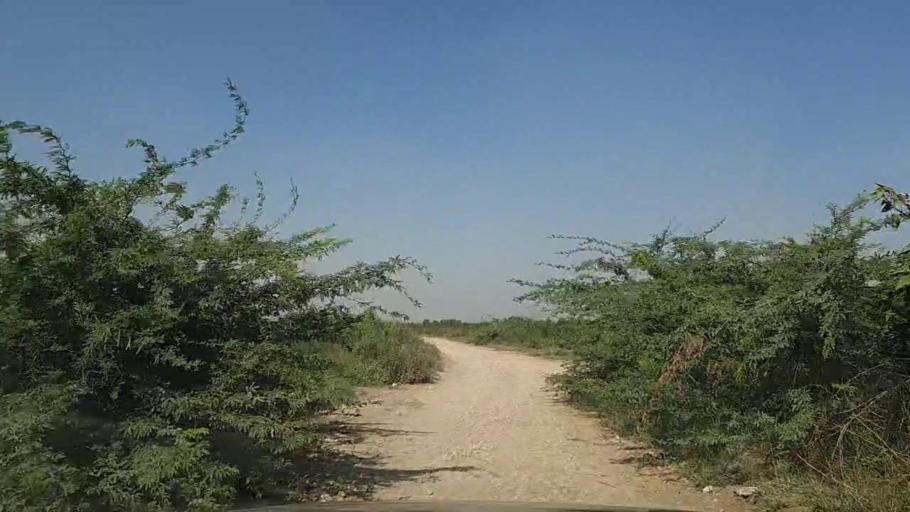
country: PK
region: Sindh
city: Daro Mehar
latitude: 24.8140
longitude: 68.1529
